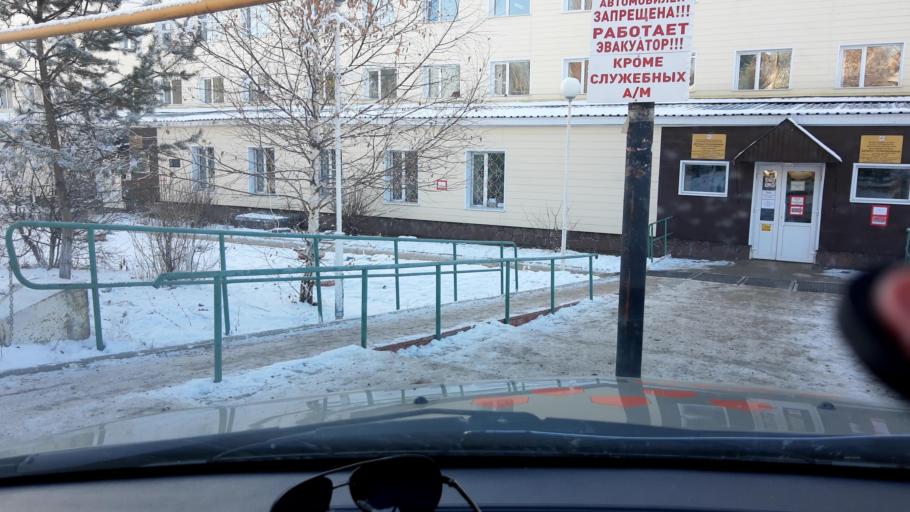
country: RU
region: Bashkortostan
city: Blagoveshchensk
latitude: 55.0466
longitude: 55.9488
